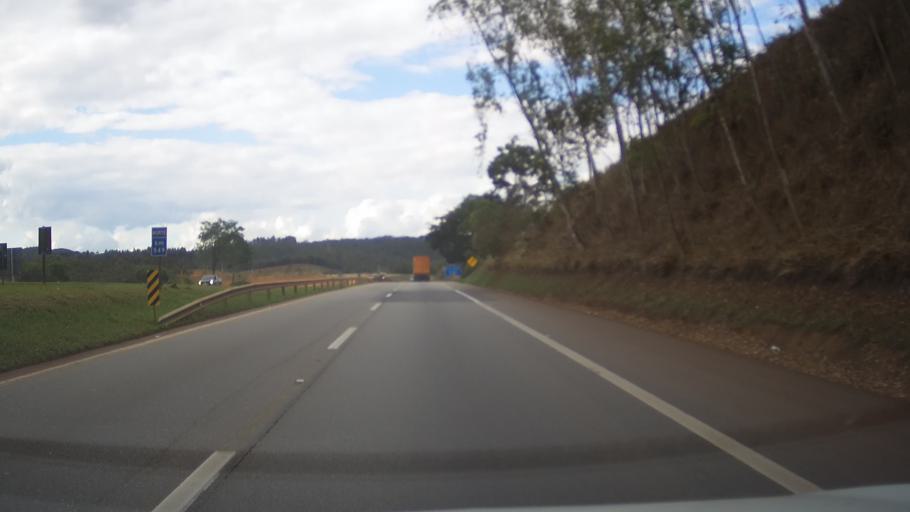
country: BR
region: Minas Gerais
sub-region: Itauna
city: Itauna
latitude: -20.2915
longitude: -44.4364
